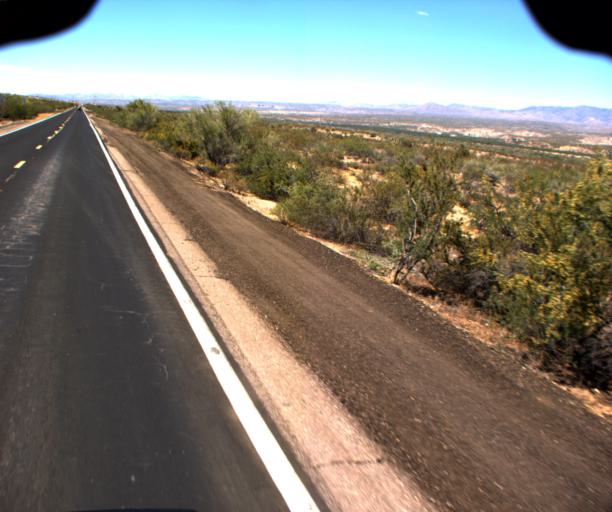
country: US
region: Arizona
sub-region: Yavapai County
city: Bagdad
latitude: 34.7212
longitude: -113.6149
